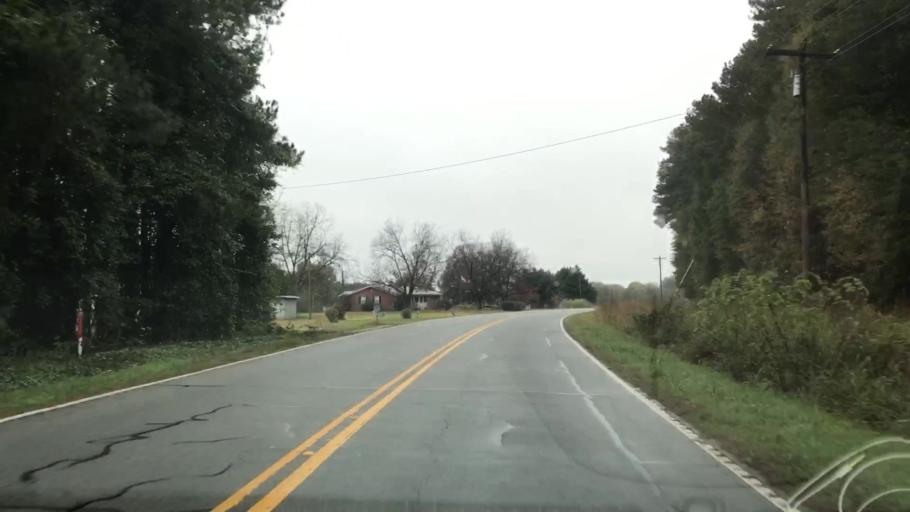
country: US
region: South Carolina
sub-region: Laurens County
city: Joanna
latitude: 34.3527
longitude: -81.7323
